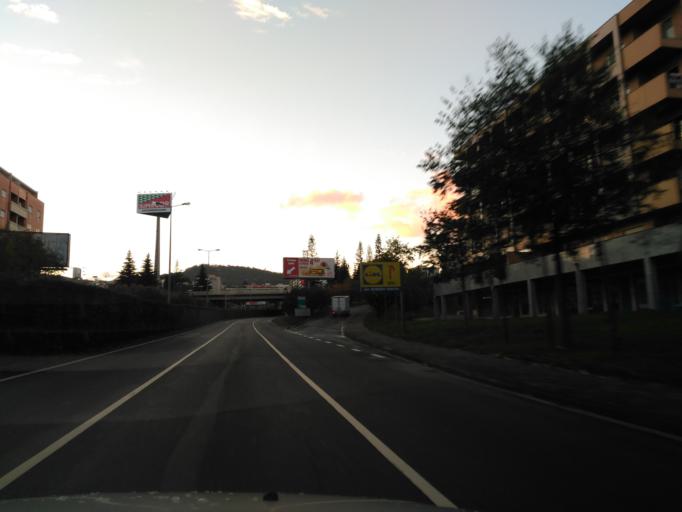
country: PT
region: Braga
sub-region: Braga
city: Braga
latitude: 41.5434
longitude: -8.4040
